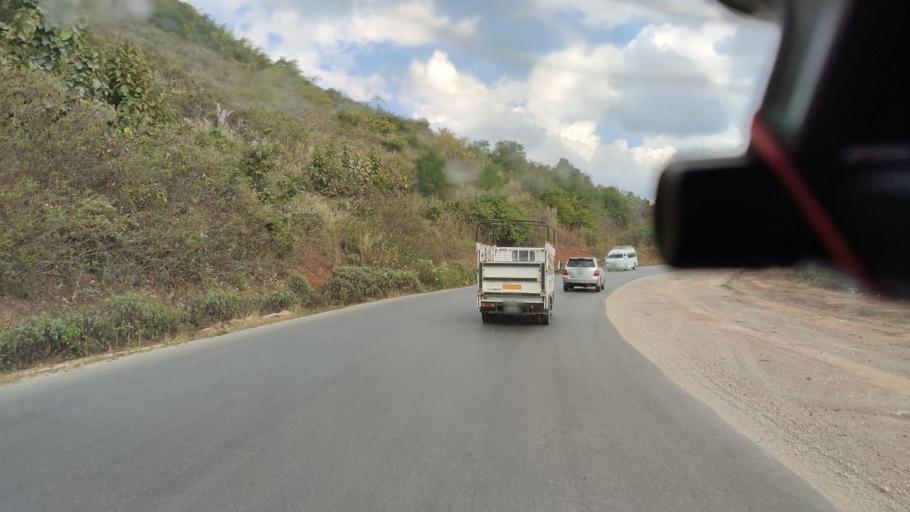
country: MM
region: Shan
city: Lashio
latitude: 23.0645
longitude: 97.7658
